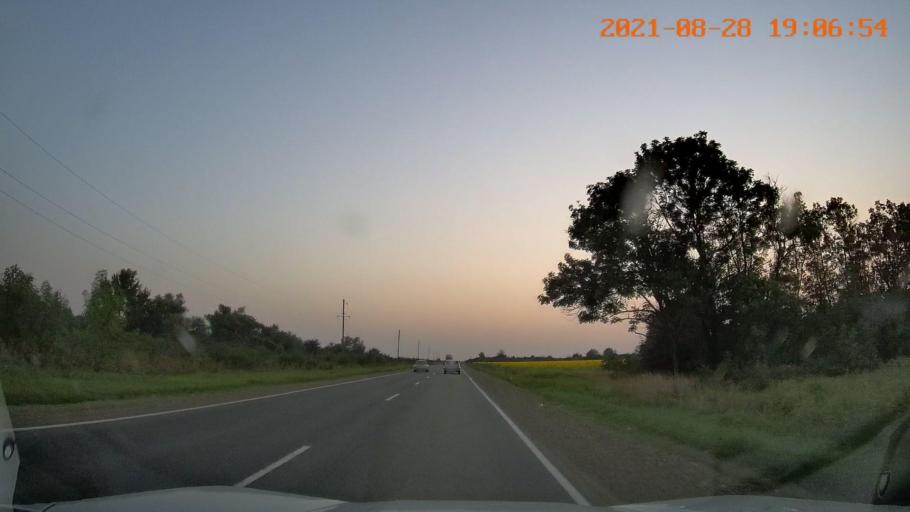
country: RU
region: Krasnodarskiy
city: Velikovechnoye
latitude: 44.8893
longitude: 39.6810
